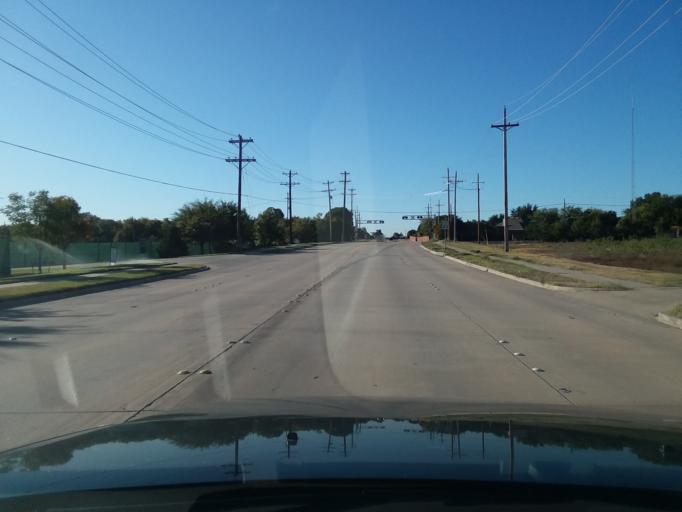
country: US
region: Texas
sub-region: Denton County
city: Highland Village
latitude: 33.0668
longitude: -97.0272
